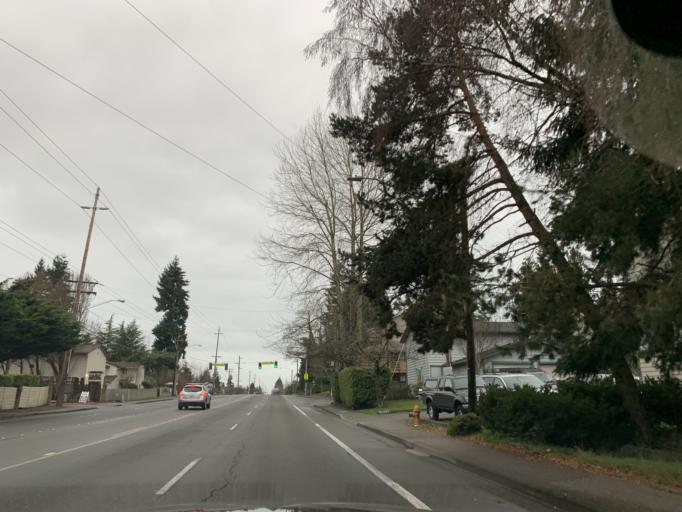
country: US
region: Washington
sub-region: Snohomish County
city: Everett
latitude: 47.9220
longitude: -122.2348
